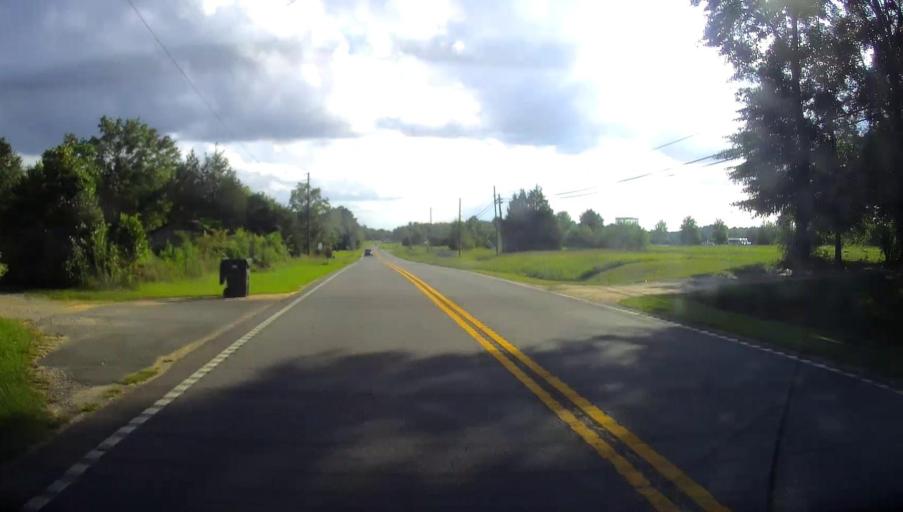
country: US
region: Georgia
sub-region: Crawford County
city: Roberta
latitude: 32.7150
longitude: -84.0184
